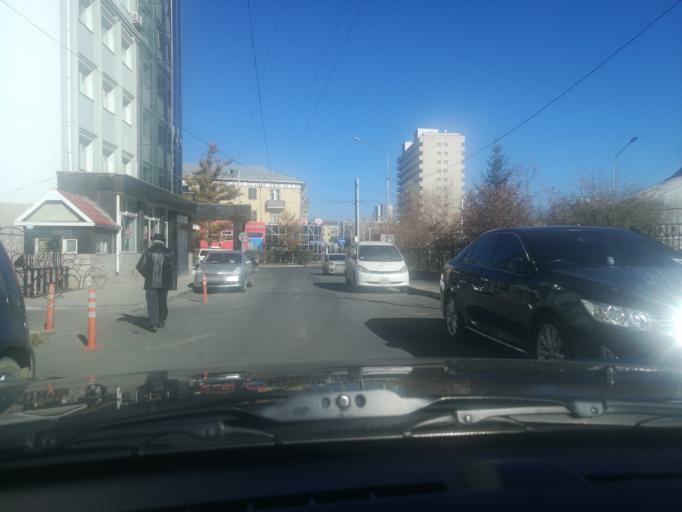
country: MN
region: Ulaanbaatar
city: Ulaanbaatar
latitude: 47.9137
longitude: 106.9092
